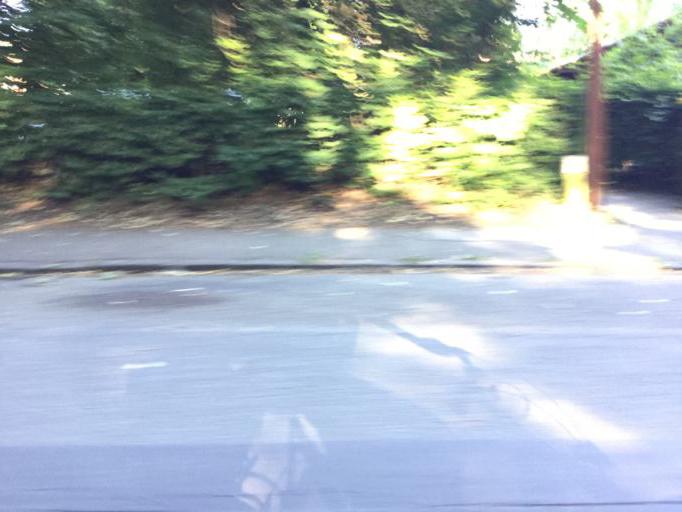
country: DE
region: Hamburg
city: Langenhorn
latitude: 53.6643
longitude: 10.0196
